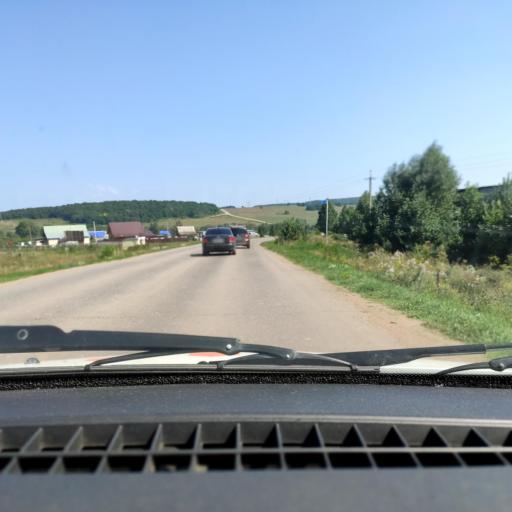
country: RU
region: Bashkortostan
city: Iglino
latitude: 54.8790
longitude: 56.5699
